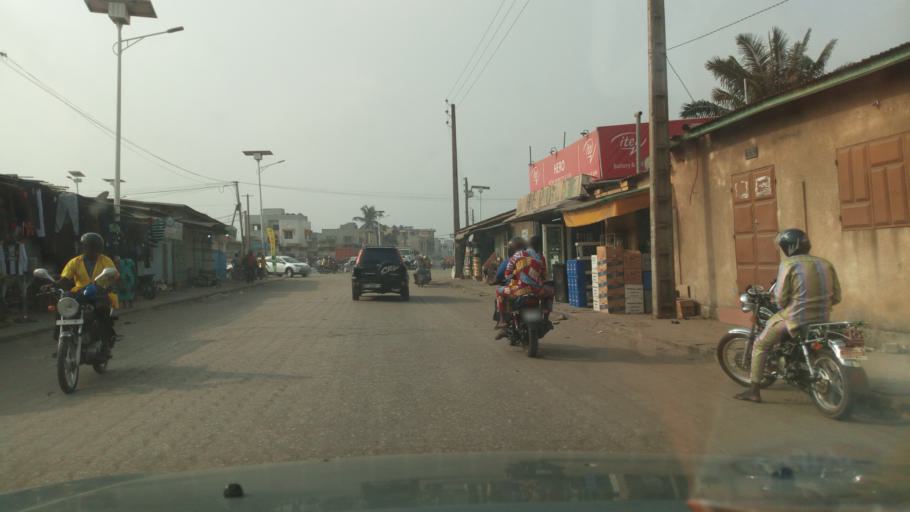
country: BJ
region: Atlantique
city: Abomey-Calavi
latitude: 6.3787
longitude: 2.3429
